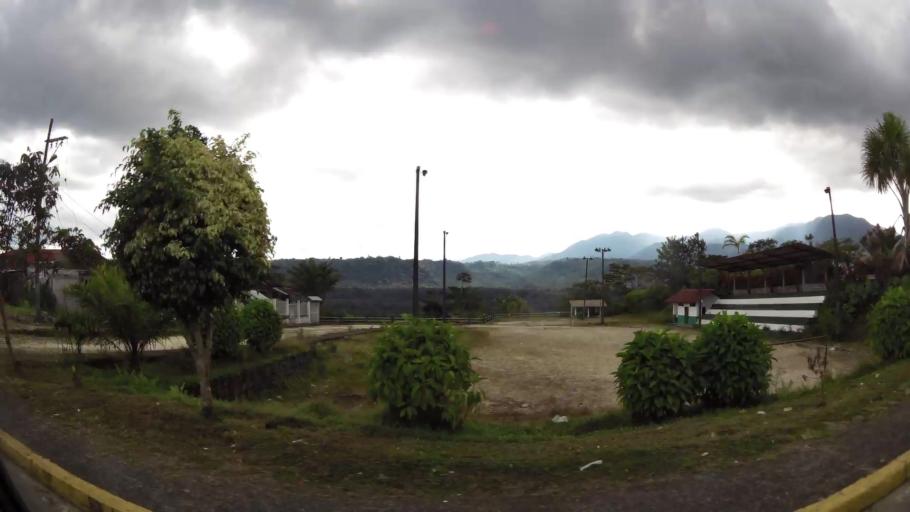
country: EC
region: Pastaza
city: Puyo
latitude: -1.4618
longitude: -78.1132
